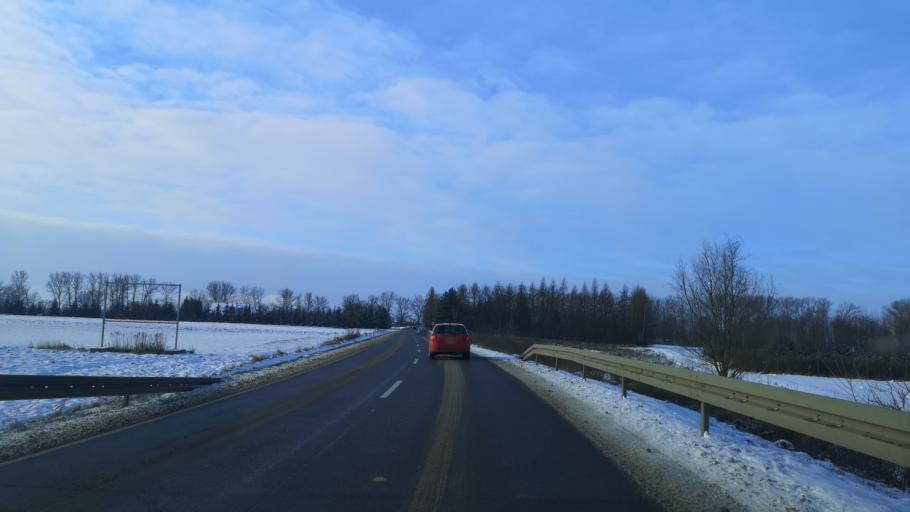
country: PL
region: Subcarpathian Voivodeship
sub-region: Powiat przeworski
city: Sieniawa
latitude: 50.1695
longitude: 22.5931
